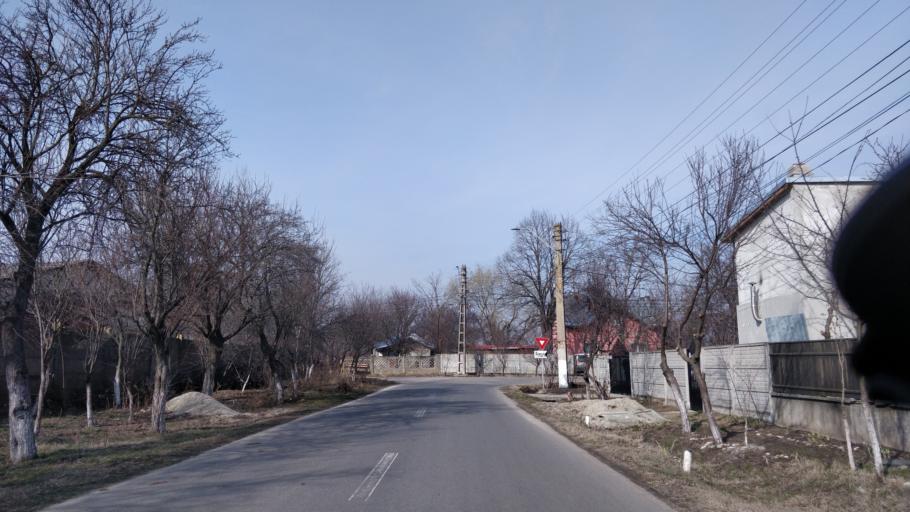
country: RO
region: Giurgiu
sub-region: Comuna Ulmi
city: Ulmi
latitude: 44.4715
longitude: 25.7694
